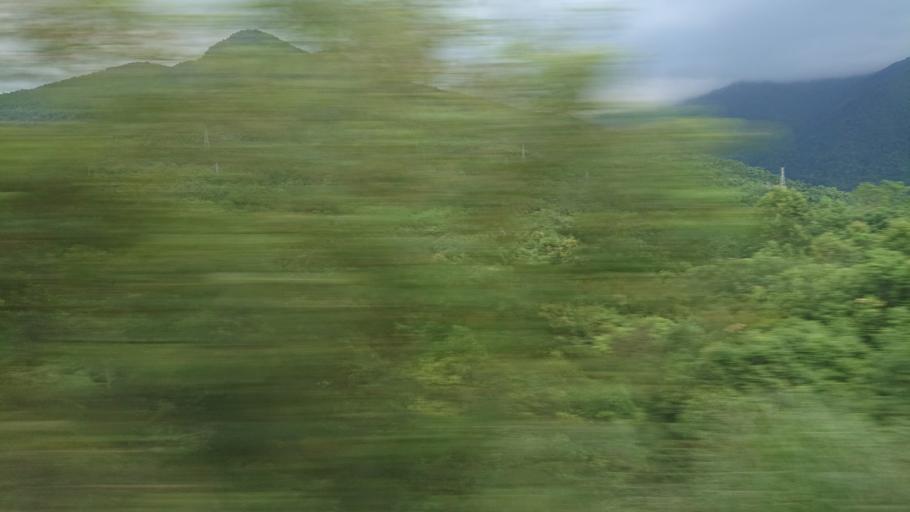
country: TW
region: Taiwan
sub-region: Hualien
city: Hualian
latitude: 23.6215
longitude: 121.3965
